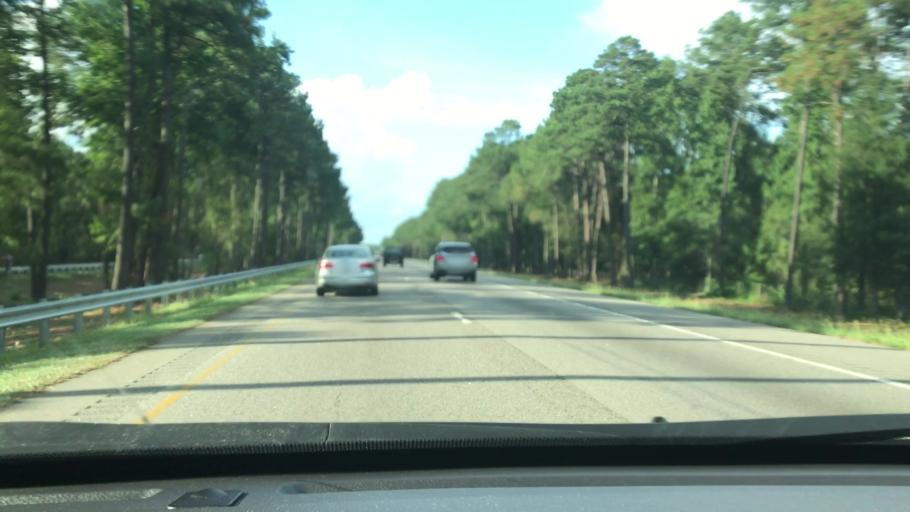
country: US
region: North Carolina
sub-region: Robeson County
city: Lumberton
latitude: 34.6837
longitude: -79.0014
